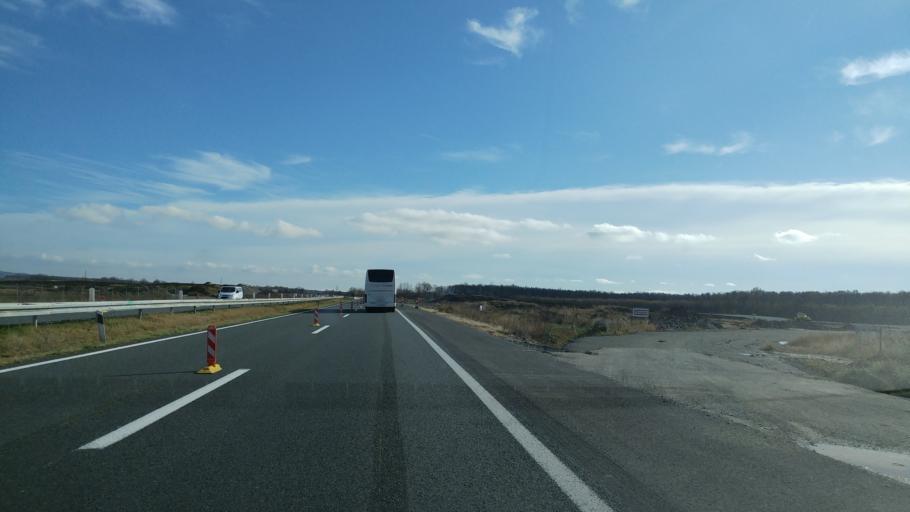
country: HR
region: Sisacko-Moslavacka
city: Lipovljani
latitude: 45.3745
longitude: 16.8799
